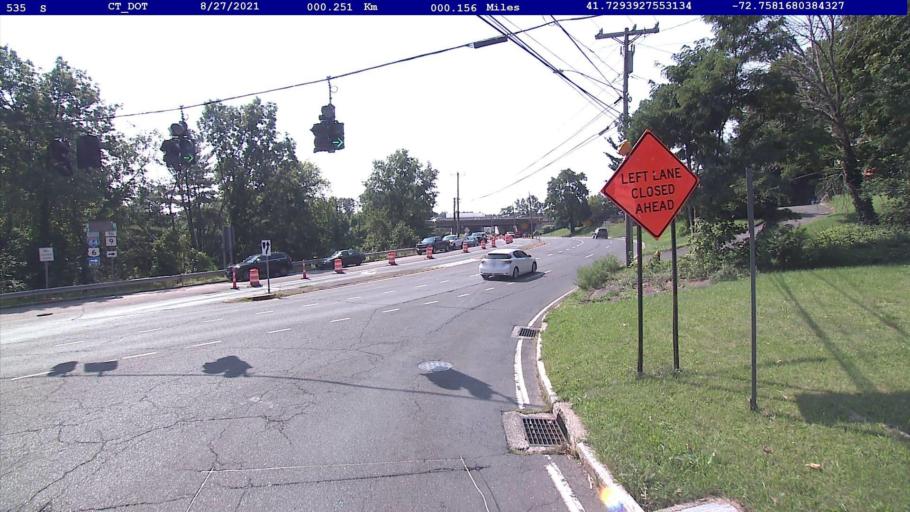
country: US
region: Connecticut
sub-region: Hartford County
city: West Hartford
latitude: 41.7294
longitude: -72.7582
